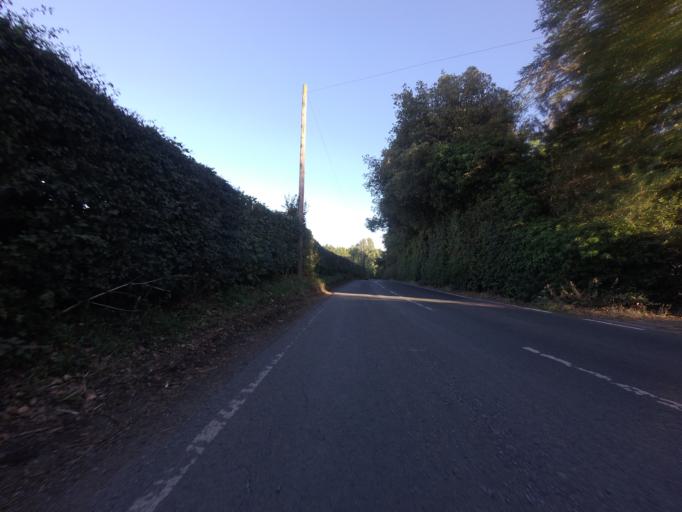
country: GB
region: England
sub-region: Kent
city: Herne Bay
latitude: 51.3324
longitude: 1.1886
